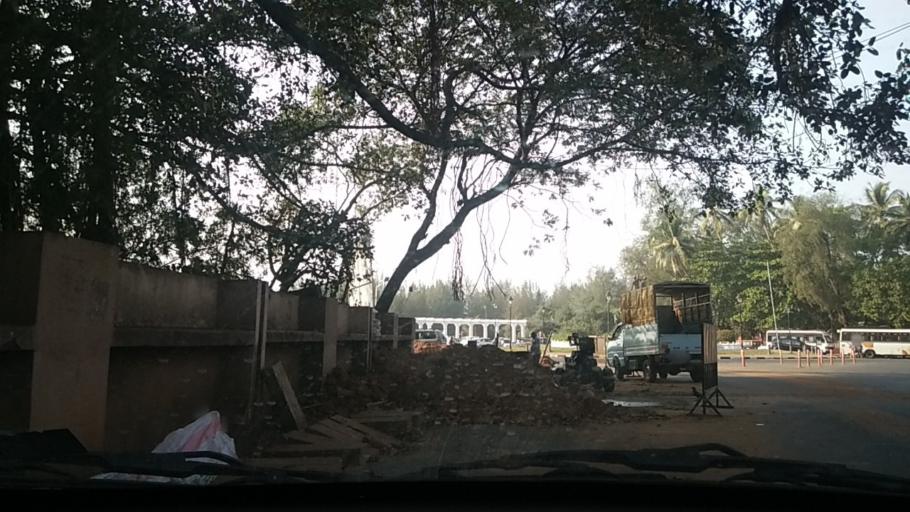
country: IN
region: Goa
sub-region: North Goa
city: Panaji
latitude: 15.4829
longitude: 73.8095
